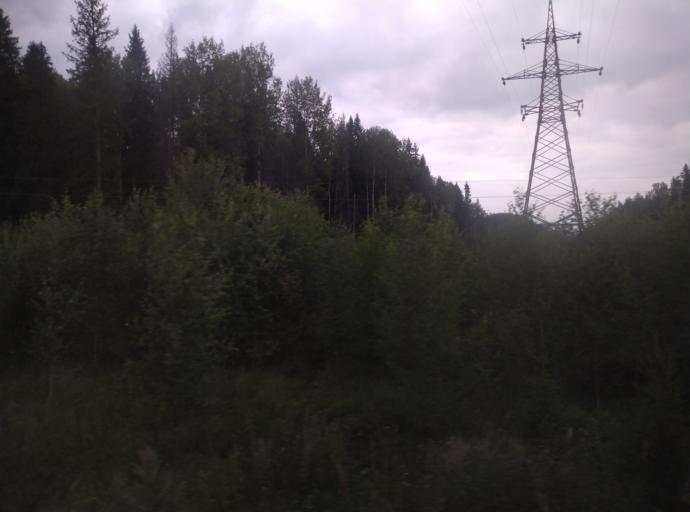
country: RU
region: Jaroslavl
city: Burmakino
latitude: 57.4368
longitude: 40.3377
